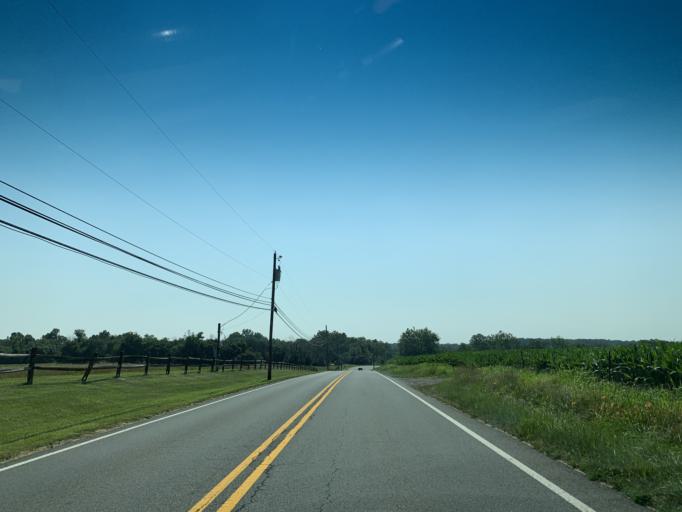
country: US
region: Maryland
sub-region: Montgomery County
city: Poolesville
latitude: 39.1247
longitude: -77.3611
